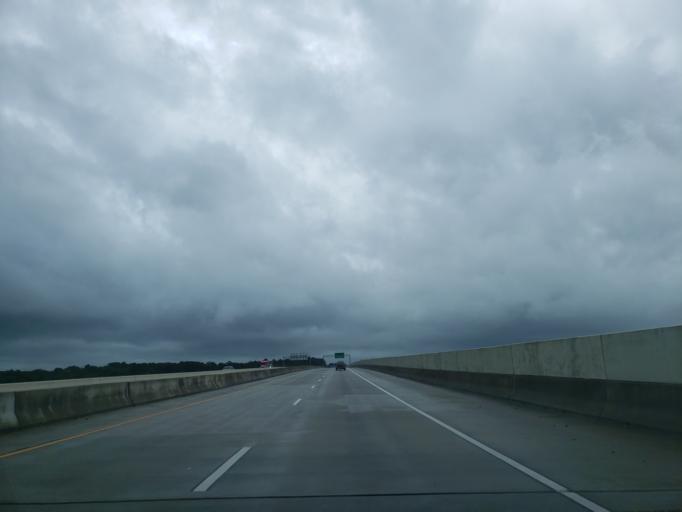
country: US
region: Georgia
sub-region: Chatham County
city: Montgomery
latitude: 31.9764
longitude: -81.1228
